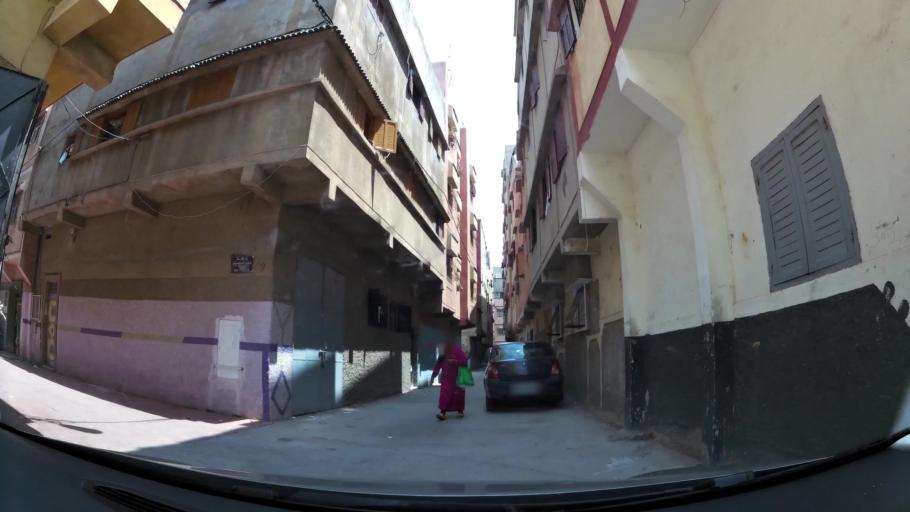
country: MA
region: Rabat-Sale-Zemmour-Zaer
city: Sale
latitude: 34.0554
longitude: -6.7823
